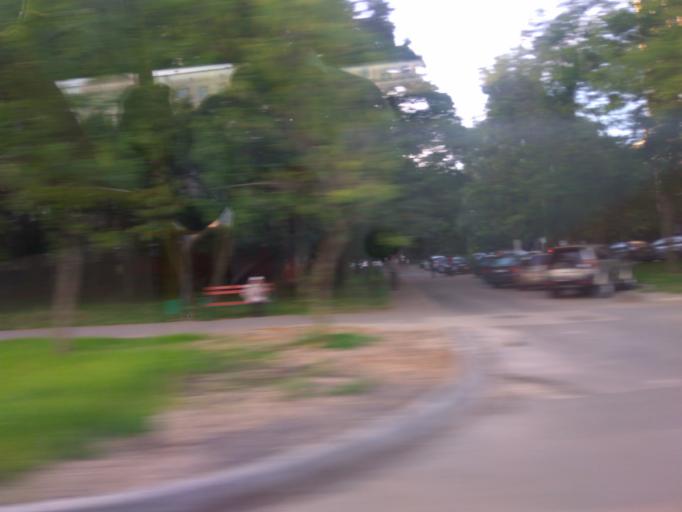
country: RU
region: Moscow
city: Chertanovo Yuzhnoye
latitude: 55.6122
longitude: 37.5964
